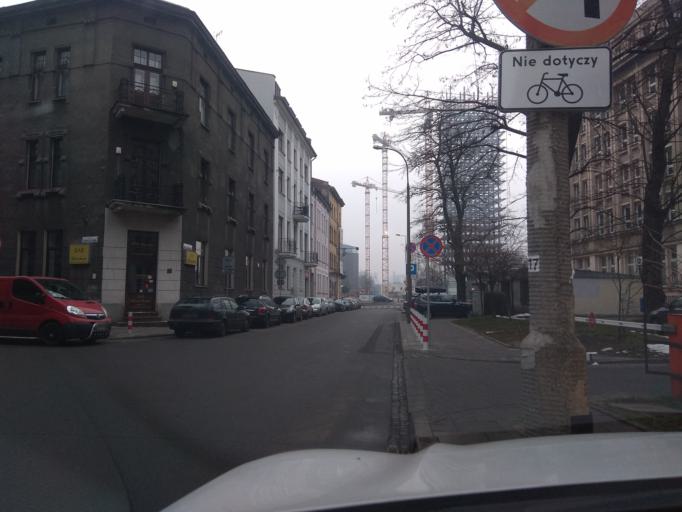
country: PL
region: Lesser Poland Voivodeship
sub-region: Krakow
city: Krakow
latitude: 50.0661
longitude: 19.9571
